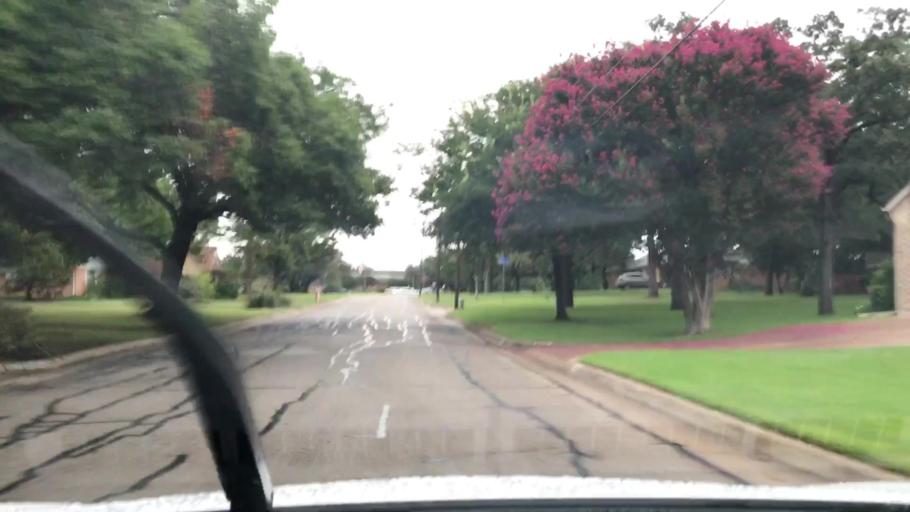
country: US
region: Texas
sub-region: Tarrant County
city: Arlington
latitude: 32.7541
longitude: -97.1246
